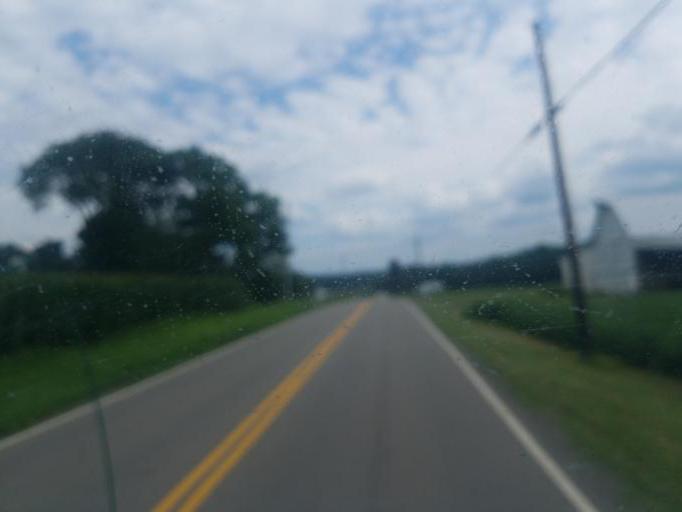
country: US
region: Ohio
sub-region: Licking County
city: Utica
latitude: 40.1634
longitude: -82.4788
